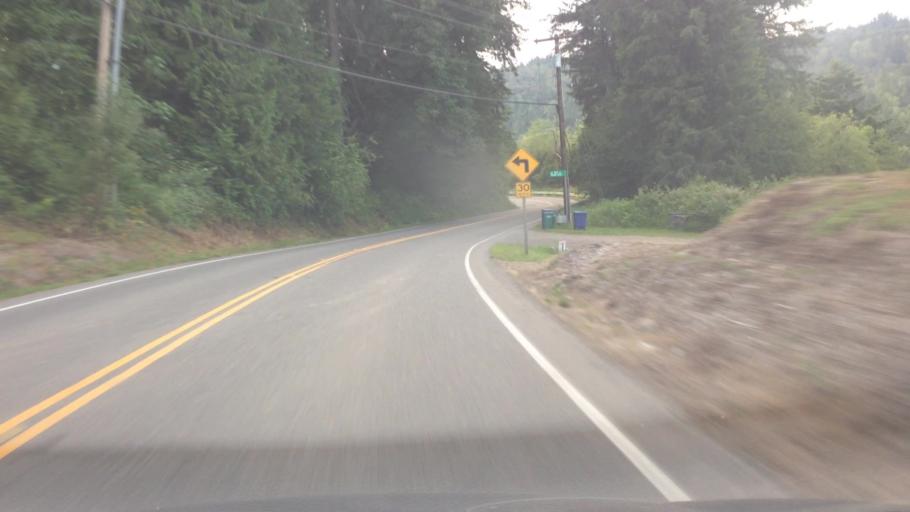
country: US
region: Washington
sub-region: King County
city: Lake Marcel-Stillwater
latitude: 47.7448
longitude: -121.9275
